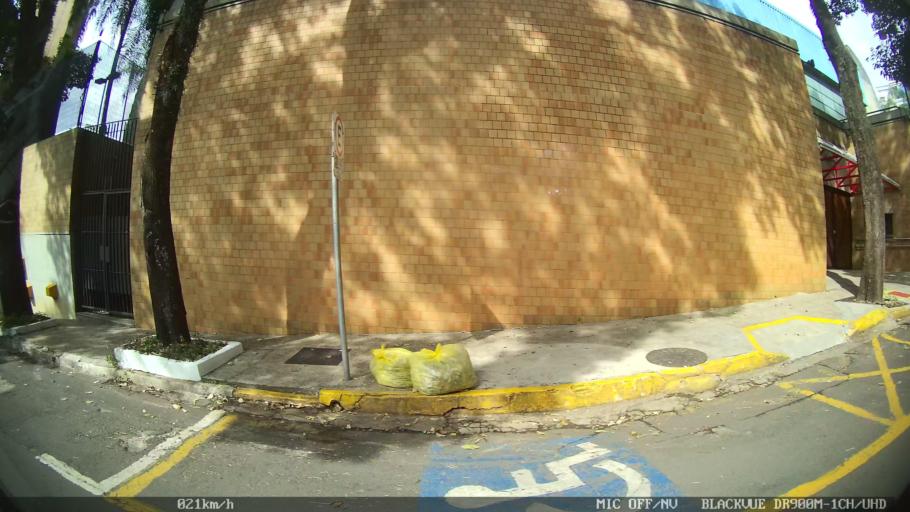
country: BR
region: Sao Paulo
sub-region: Piracicaba
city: Piracicaba
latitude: -22.7265
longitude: -47.6570
